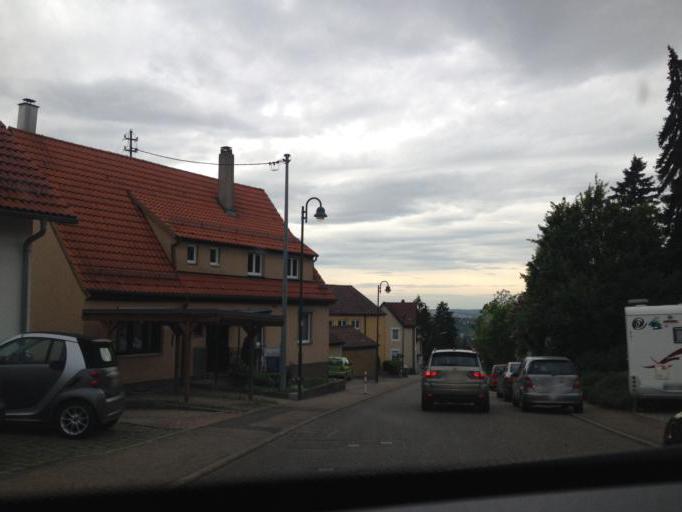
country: DE
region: Baden-Wuerttemberg
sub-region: Regierungsbezirk Stuttgart
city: Esslingen
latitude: 48.7482
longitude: 9.3418
